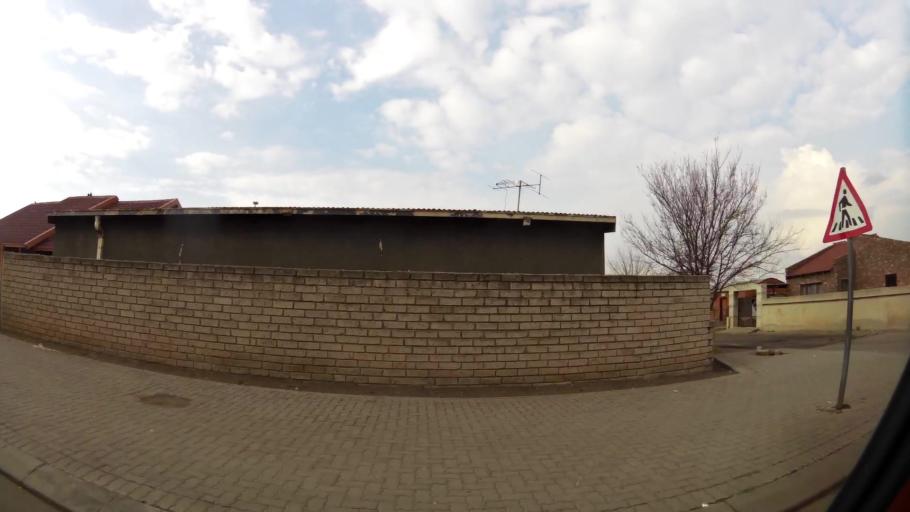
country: ZA
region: Gauteng
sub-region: Sedibeng District Municipality
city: Vanderbijlpark
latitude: -26.6866
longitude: 27.8691
